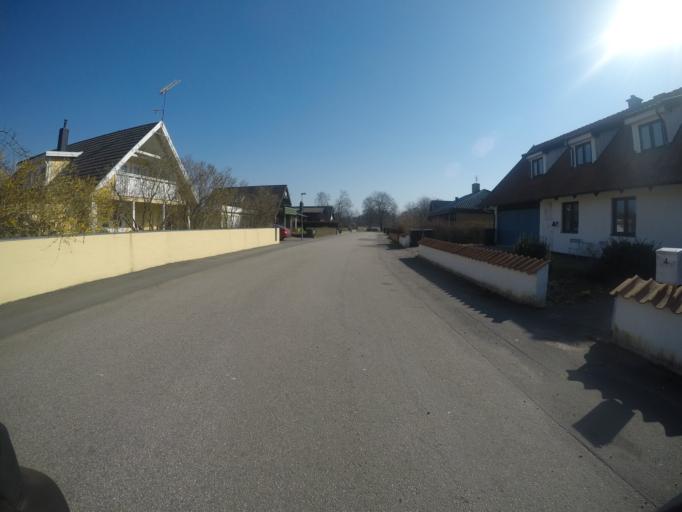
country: SE
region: Halland
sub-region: Laholms Kommun
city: Laholm
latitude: 56.5008
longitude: 13.0461
